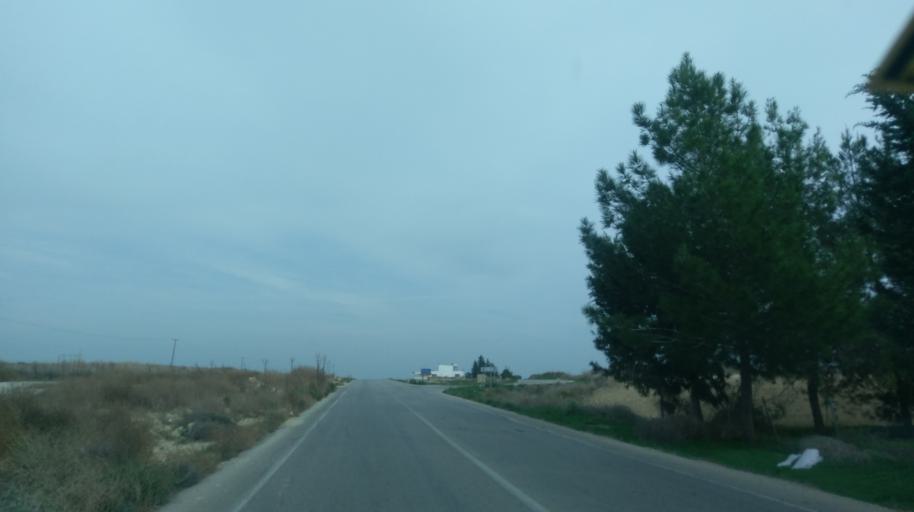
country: CY
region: Ammochostos
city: Trikomo
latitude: 35.3619
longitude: 34.0157
